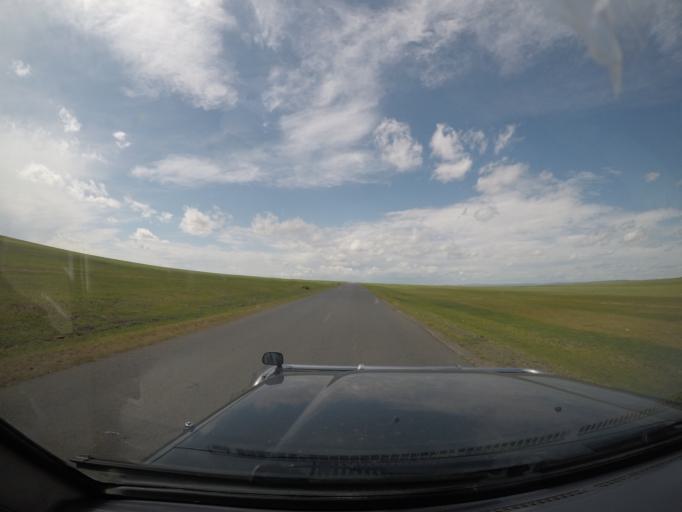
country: MN
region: Hentiy
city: Moron
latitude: 47.4081
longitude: 110.2319
